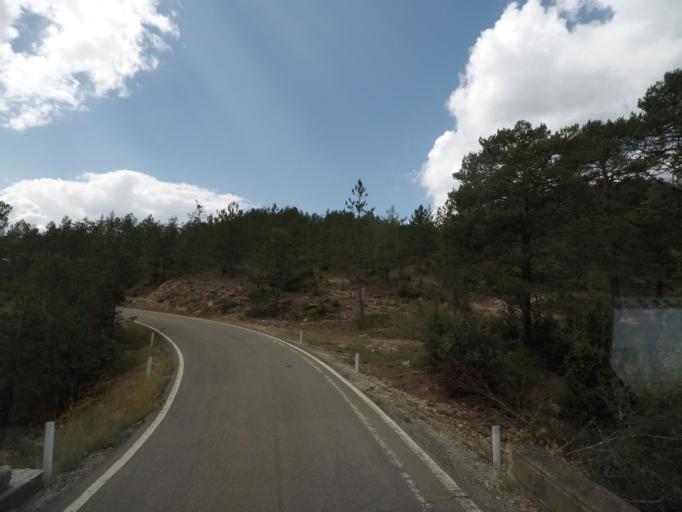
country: ES
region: Aragon
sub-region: Provincia de Huesca
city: Fiscal
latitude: 42.4081
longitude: -0.1642
